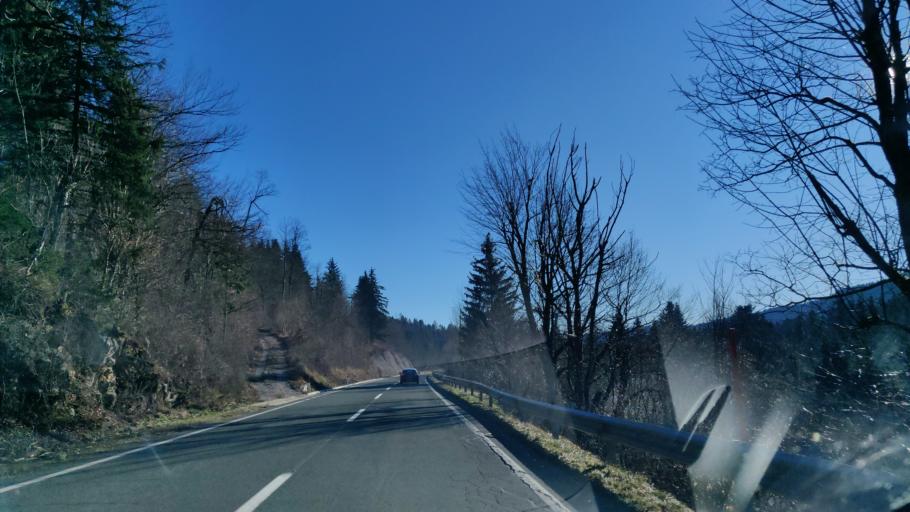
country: SI
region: Logatec
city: Logatec
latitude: 45.8882
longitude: 14.1977
